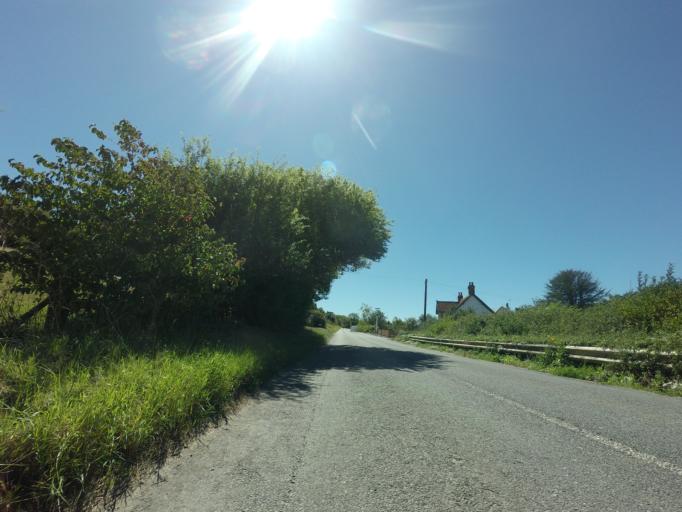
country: GB
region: England
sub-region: Kent
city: Eastry
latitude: 51.2121
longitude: 1.2997
